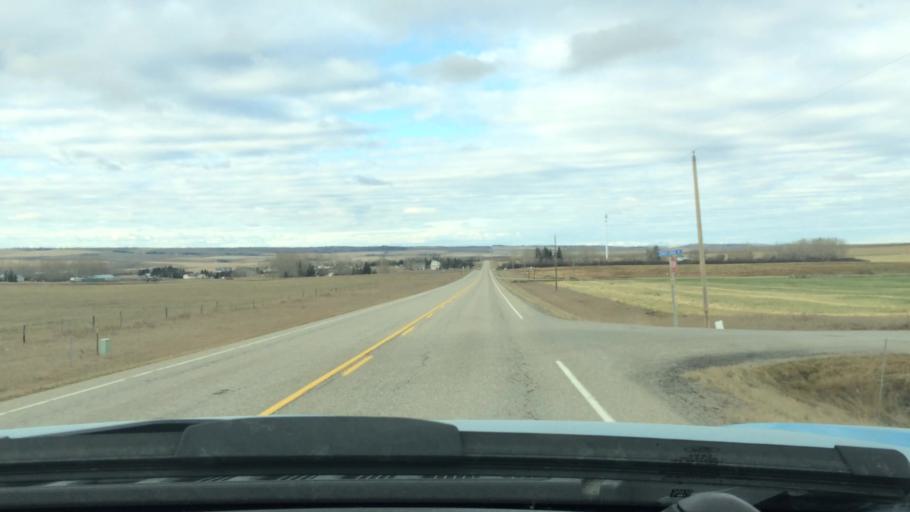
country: CA
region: Alberta
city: Airdrie
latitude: 51.2115
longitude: -114.1356
